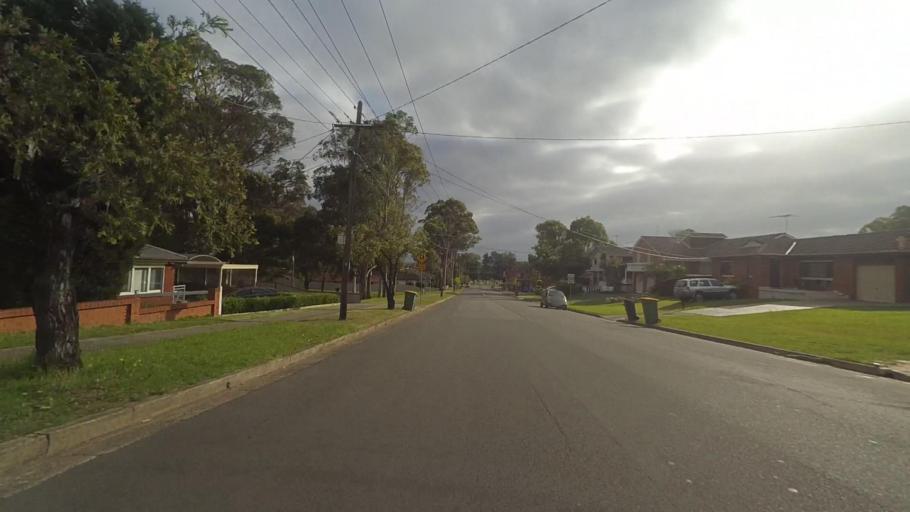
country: AU
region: New South Wales
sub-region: Bankstown
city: Milperra
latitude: -33.9142
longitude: 150.9992
